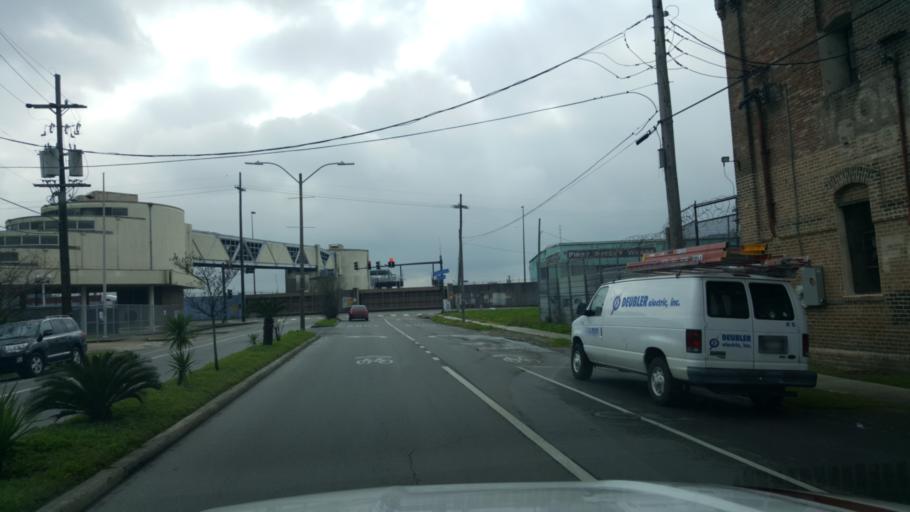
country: US
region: Louisiana
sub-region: Jefferson Parish
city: Gretna
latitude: 29.9240
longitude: -90.0719
